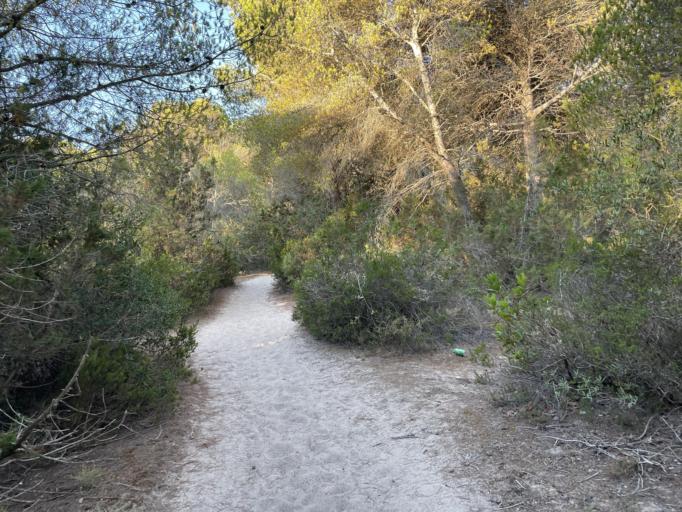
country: ES
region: Balearic Islands
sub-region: Illes Balears
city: Capdepera
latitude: 39.7180
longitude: 3.4530
